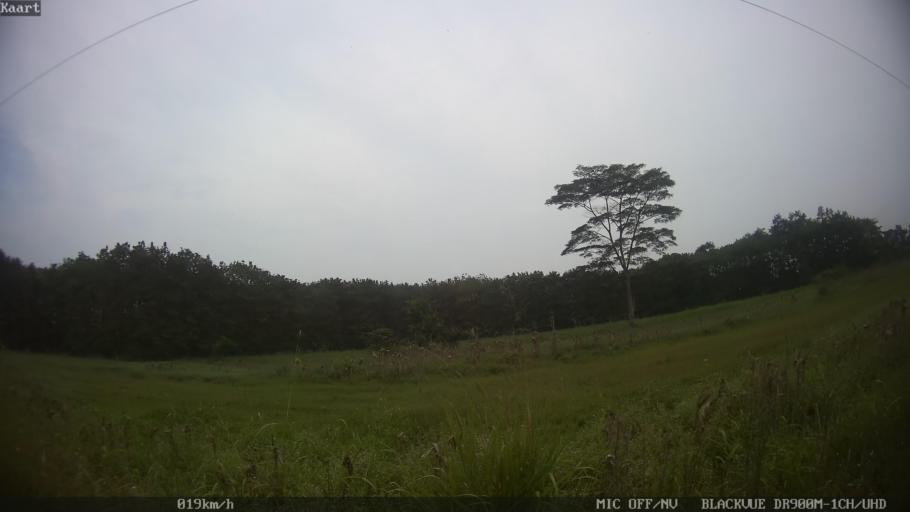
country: ID
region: Lampung
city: Panjang
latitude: -5.4083
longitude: 105.3574
